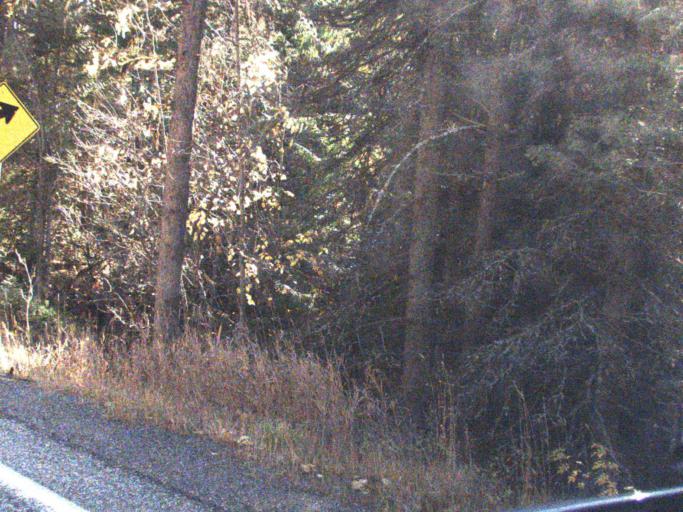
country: US
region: Washington
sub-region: Stevens County
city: Kettle Falls
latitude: 48.6036
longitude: -118.3597
